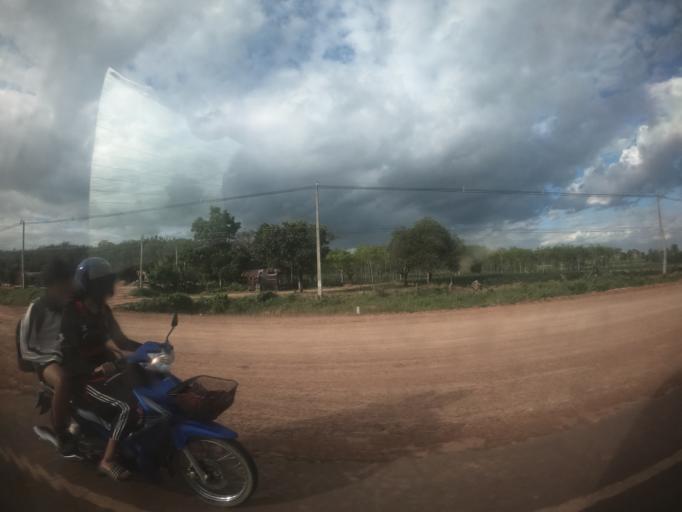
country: TH
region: Surin
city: Kap Choeng
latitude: 14.4940
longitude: 103.5705
